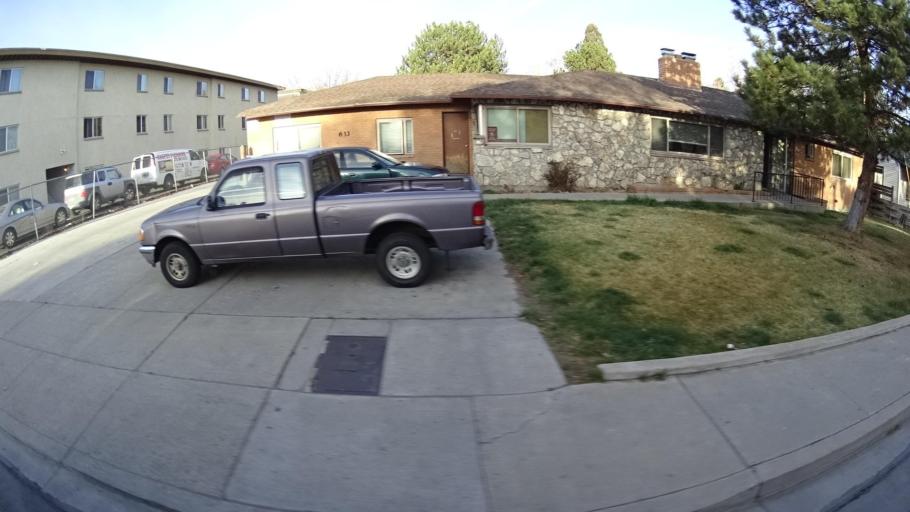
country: US
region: Nevada
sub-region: Washoe County
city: Sparks
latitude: 39.5392
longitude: -119.7715
